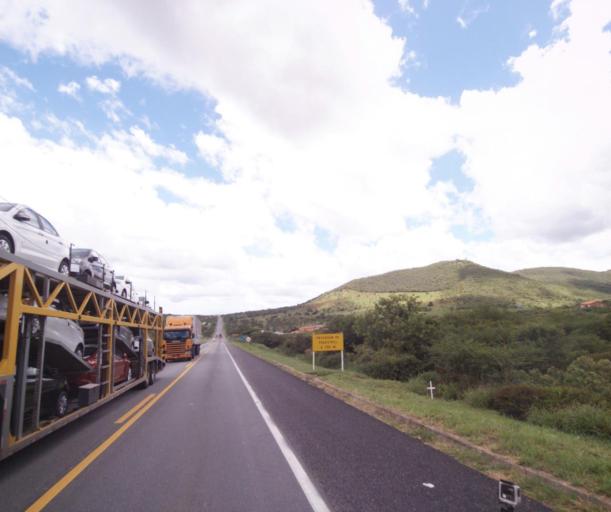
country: BR
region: Bahia
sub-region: Pocoes
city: Pocoes
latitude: -14.3539
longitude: -40.3357
